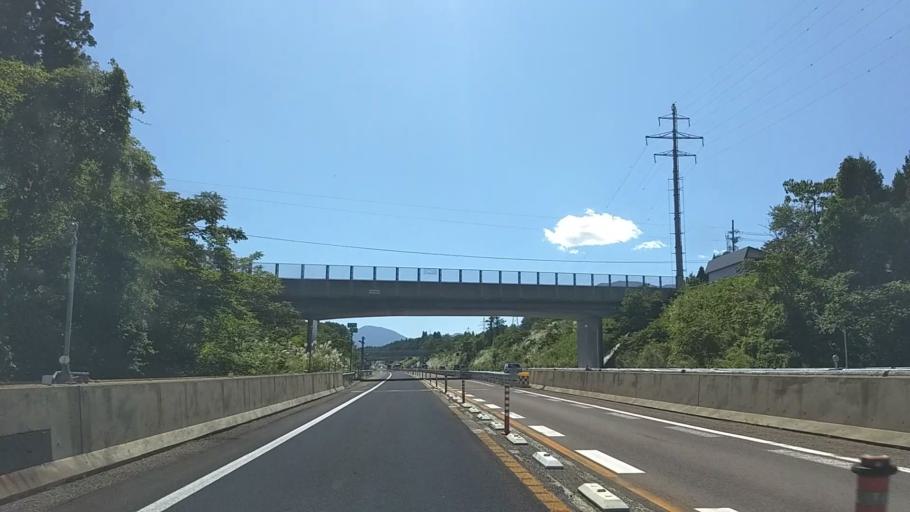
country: JP
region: Niigata
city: Arai
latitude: 36.8891
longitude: 138.2018
